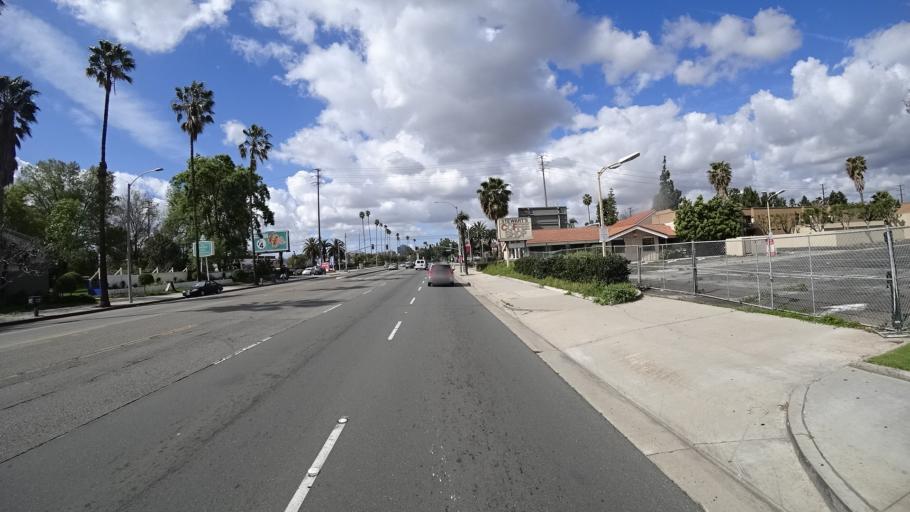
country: US
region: California
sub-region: Orange County
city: Anaheim
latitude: 33.8382
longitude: -117.9013
